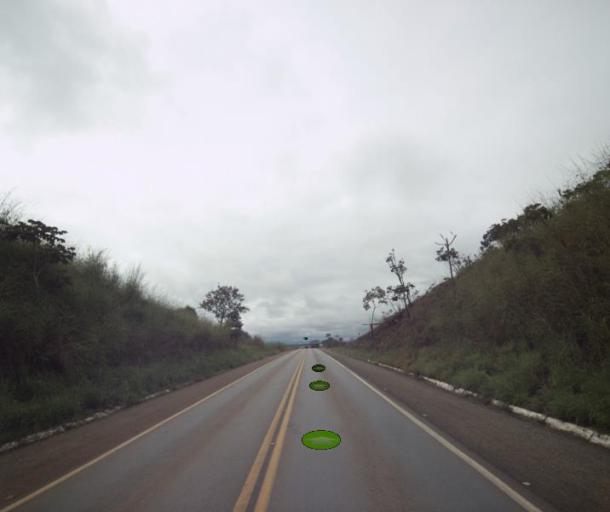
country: BR
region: Goias
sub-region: Uruacu
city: Uruacu
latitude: -14.6753
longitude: -49.1373
